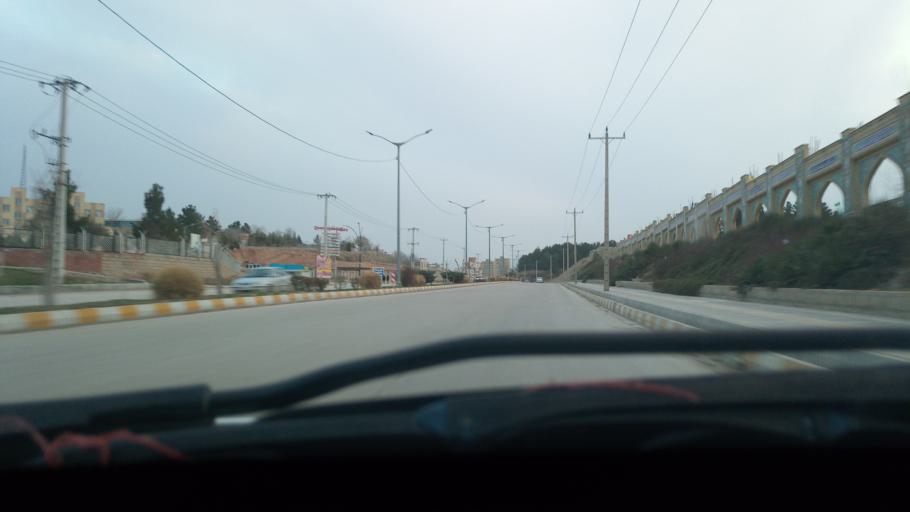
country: IR
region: Khorasan-e Shomali
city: Bojnurd
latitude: 37.4598
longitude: 57.3319
